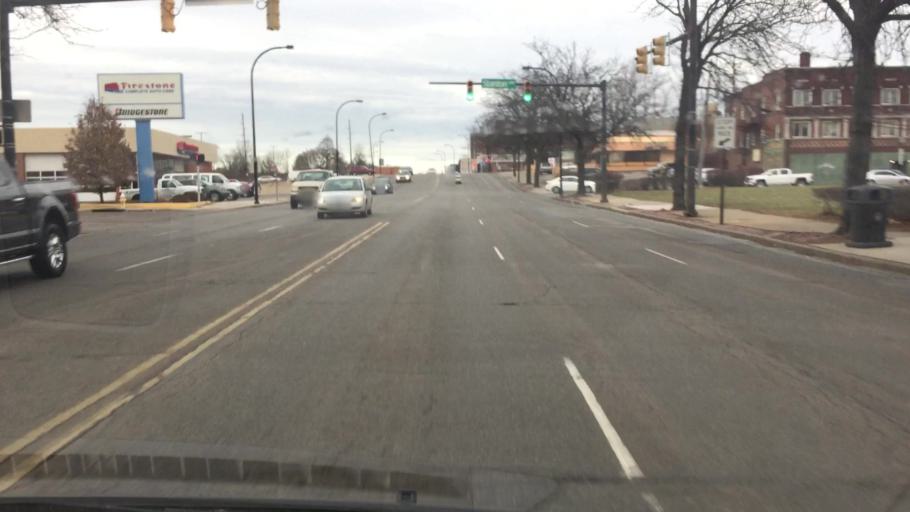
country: US
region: Ohio
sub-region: Summit County
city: Akron
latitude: 41.0524
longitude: -81.5281
